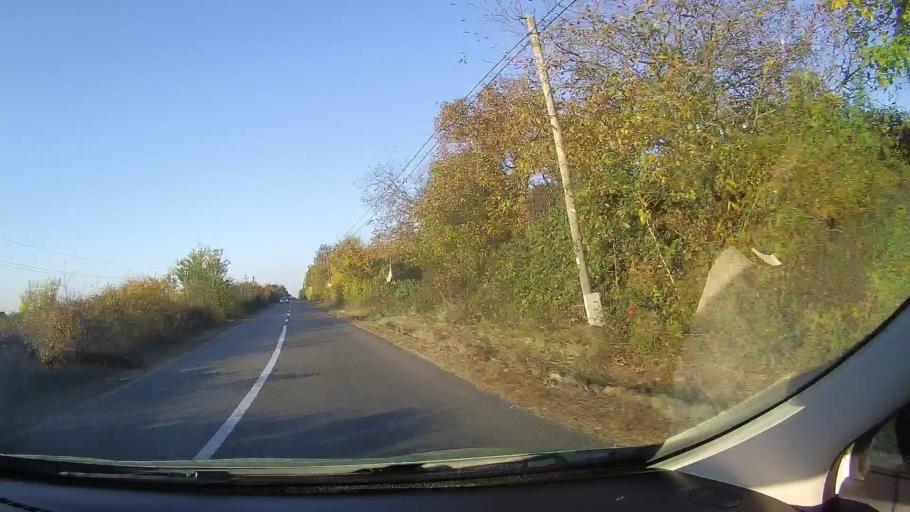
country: RO
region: Bihor
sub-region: Comuna Paleu
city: Paleu
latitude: 47.1032
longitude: 21.9288
